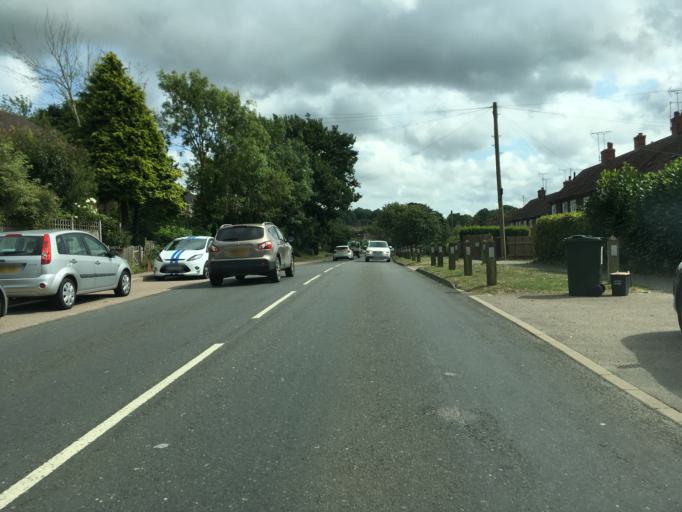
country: GB
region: England
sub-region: Kent
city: Tenterden
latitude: 51.0830
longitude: 0.6932
